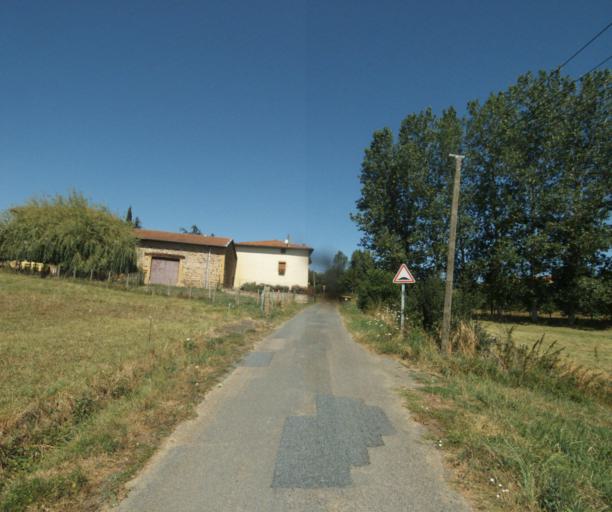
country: FR
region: Rhone-Alpes
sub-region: Departement du Rhone
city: Bessenay
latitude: 45.7930
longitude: 4.5572
